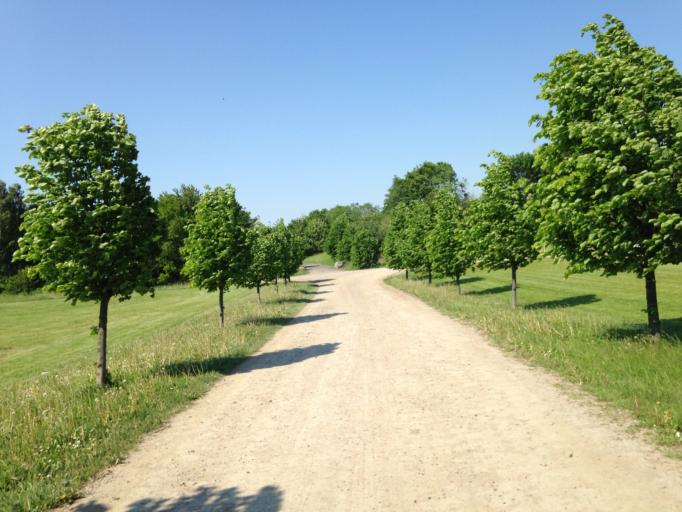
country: SE
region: Skane
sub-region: Malmo
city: Tygelsjo
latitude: 55.5520
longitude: 13.0120
